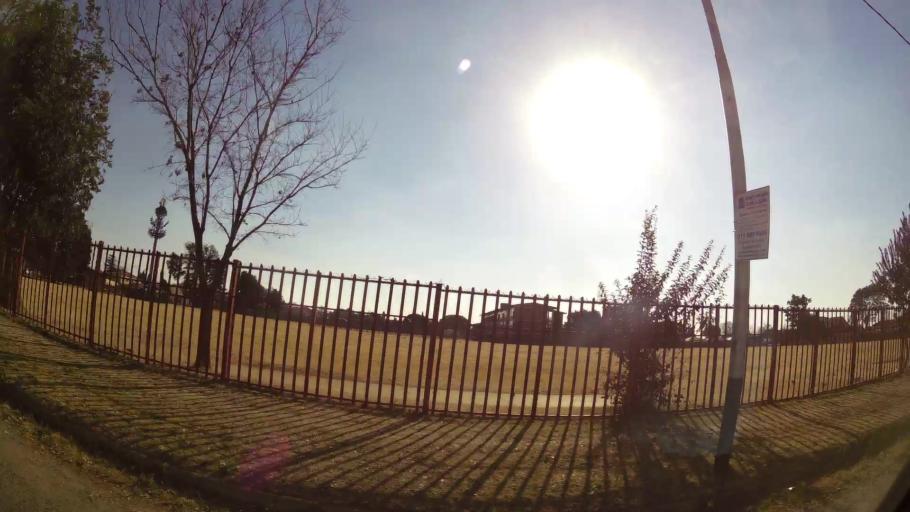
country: ZA
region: Gauteng
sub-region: City of Johannesburg Metropolitan Municipality
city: Johannesburg
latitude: -26.2552
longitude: 28.0125
